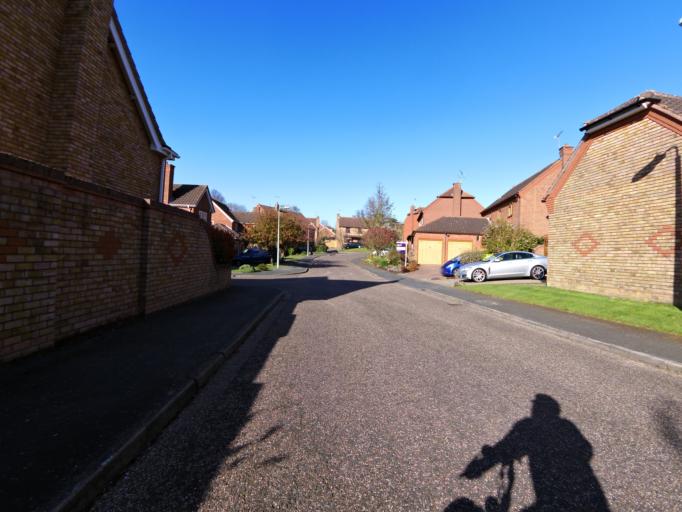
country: GB
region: England
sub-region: Suffolk
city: Bramford
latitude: 52.0565
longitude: 1.1150
